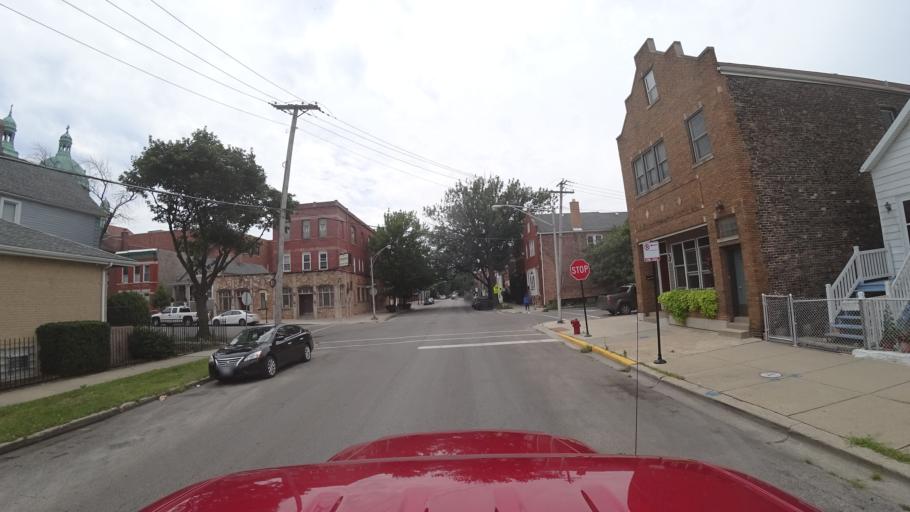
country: US
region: Illinois
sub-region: Cook County
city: Chicago
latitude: 41.8364
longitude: -87.6536
